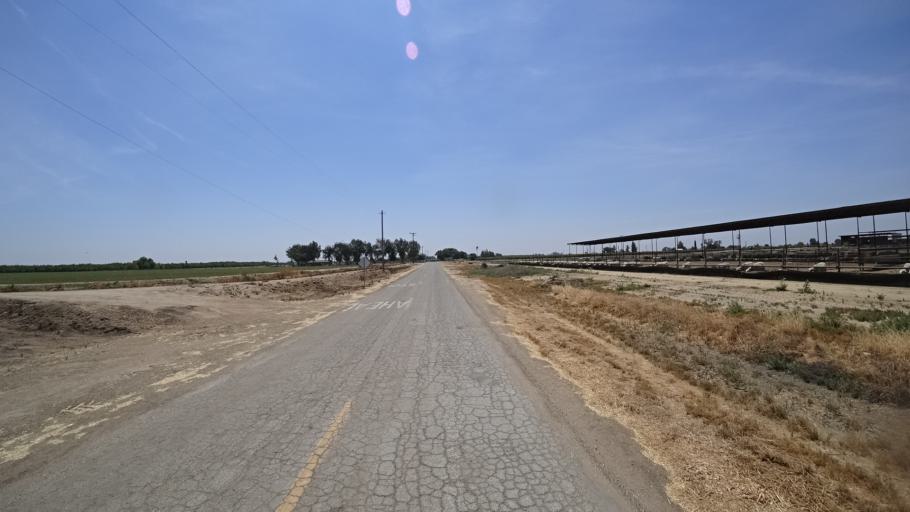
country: US
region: California
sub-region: Fresno County
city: Riverdale
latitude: 36.4009
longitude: -119.8164
